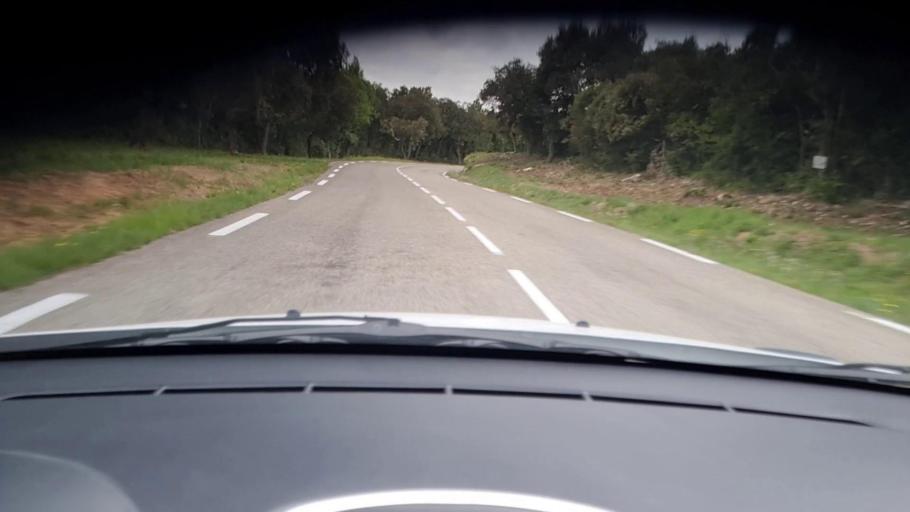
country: FR
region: Languedoc-Roussillon
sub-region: Departement du Gard
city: Poulx
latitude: 43.9211
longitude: 4.3918
